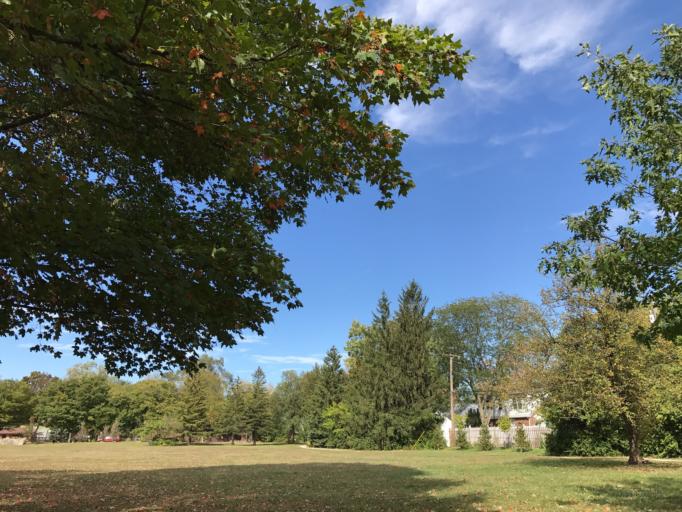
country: US
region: Michigan
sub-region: Washtenaw County
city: Ann Arbor
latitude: 42.2595
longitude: -83.7347
